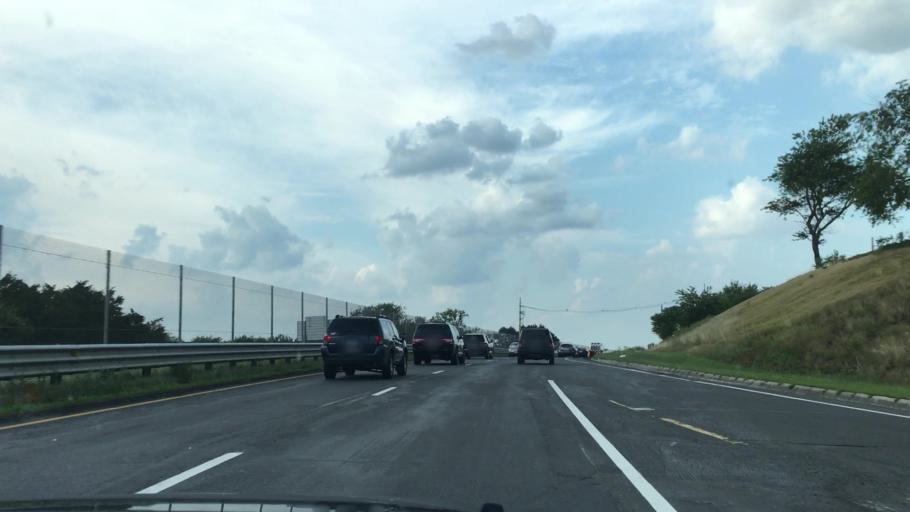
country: US
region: Massachusetts
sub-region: Essex County
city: Peabody
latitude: 42.5513
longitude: -70.9361
